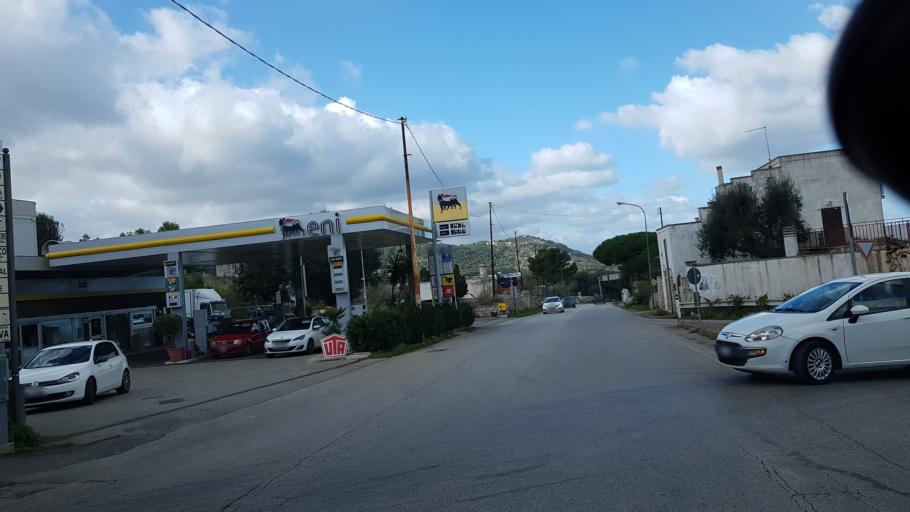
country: IT
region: Apulia
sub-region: Provincia di Brindisi
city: Ostuni
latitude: 40.7326
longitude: 17.5689
